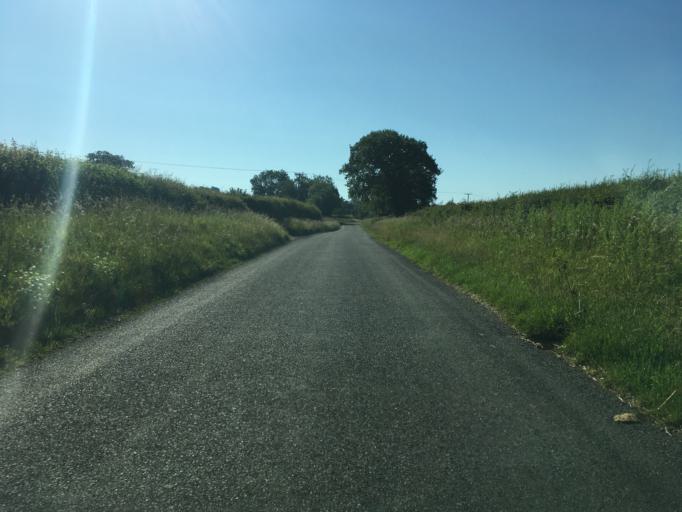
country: GB
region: England
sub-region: South Gloucestershire
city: Hinton
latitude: 51.4876
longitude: -2.3933
